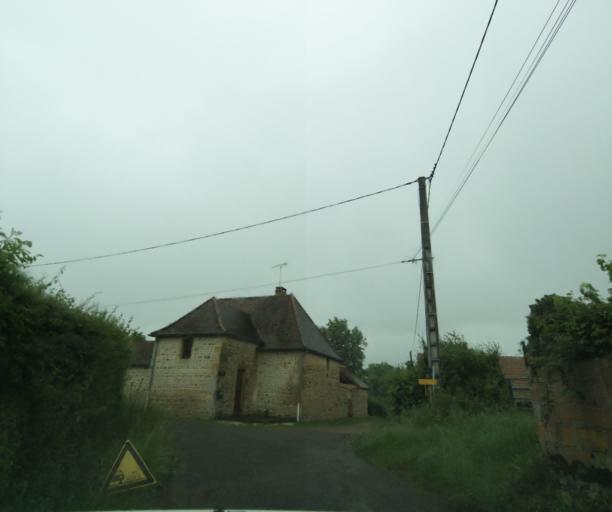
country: FR
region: Bourgogne
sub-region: Departement de Saone-et-Loire
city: Charolles
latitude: 46.3515
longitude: 4.1984
